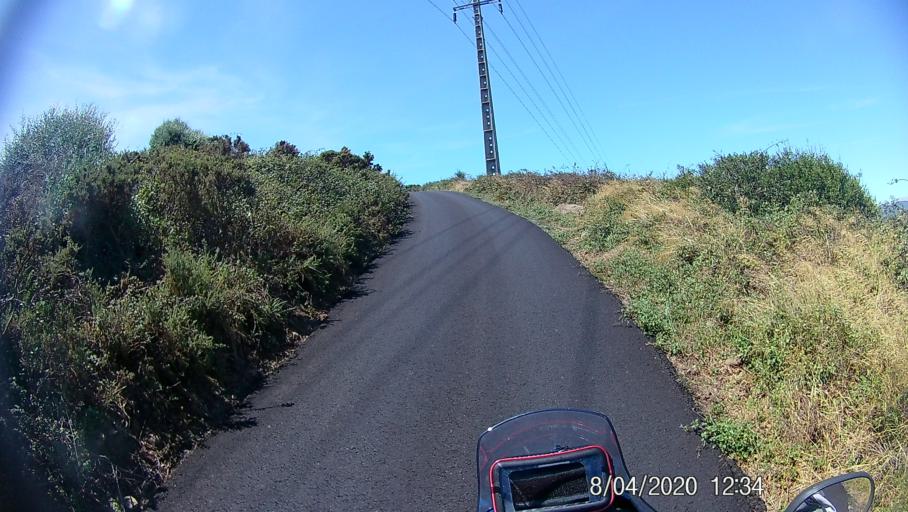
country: PT
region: Lisbon
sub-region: Sintra
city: Rio de Mouro
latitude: 38.7510
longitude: -9.3615
